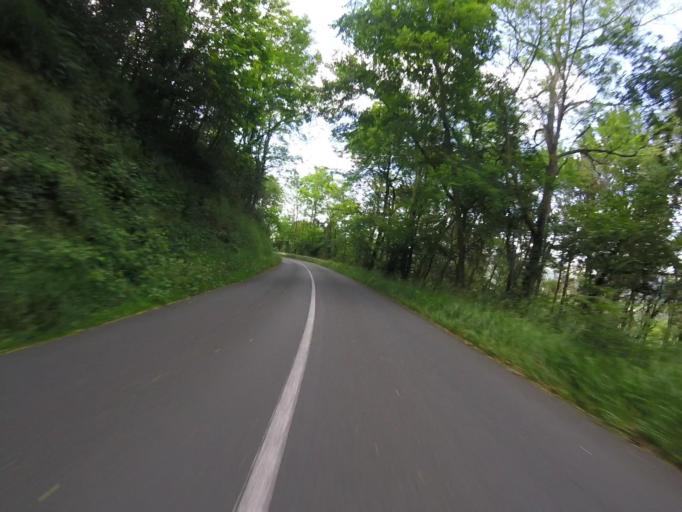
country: ES
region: Basque Country
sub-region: Provincia de Guipuzcoa
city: Errenteria
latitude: 43.2768
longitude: -1.8526
